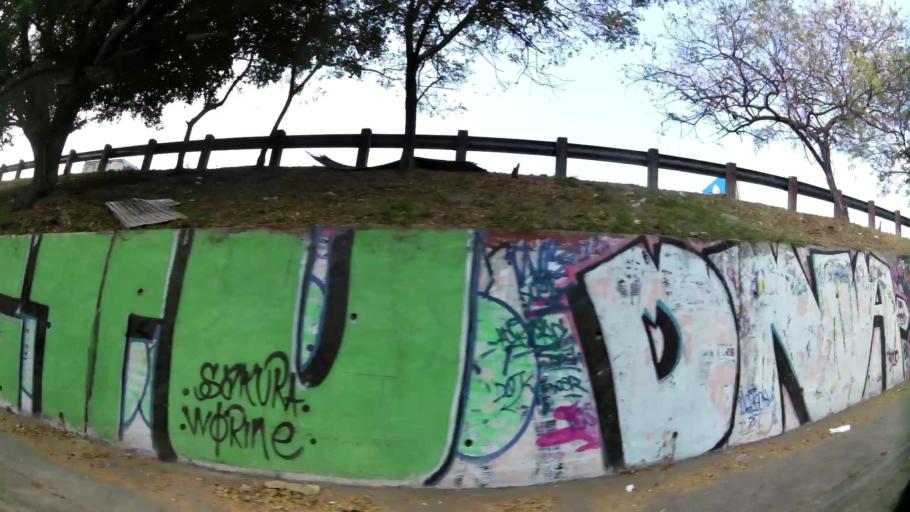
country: SV
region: San Salvador
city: Soyapango
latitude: 13.7162
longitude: -89.1402
